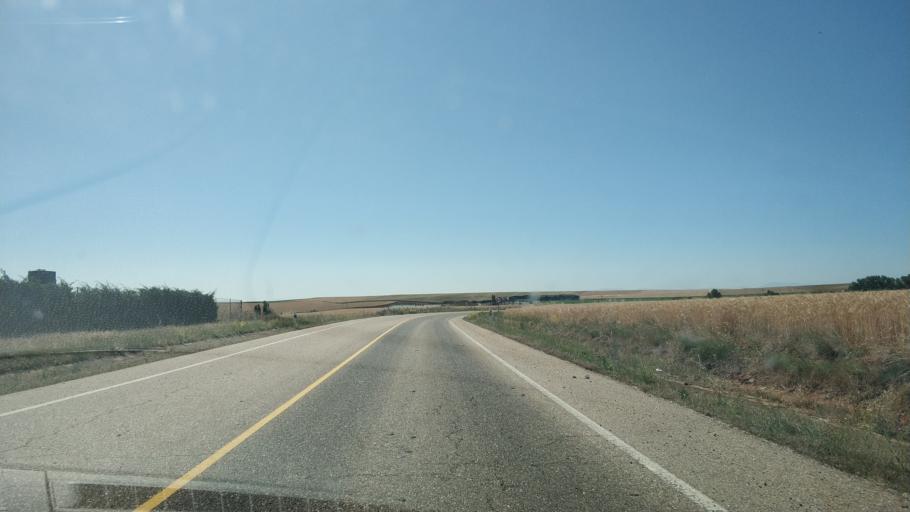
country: ES
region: Castille and Leon
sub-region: Provincia de Zamora
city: Canizal
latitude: 41.1633
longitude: -5.4006
